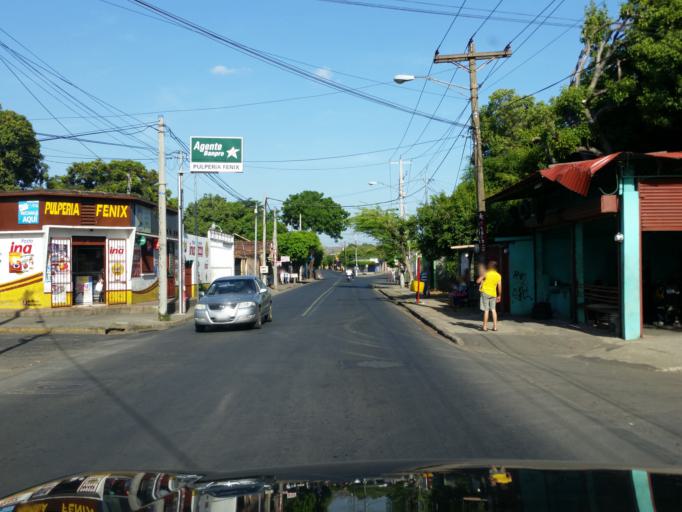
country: NI
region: Managua
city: Managua
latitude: 12.1553
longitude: -86.2931
